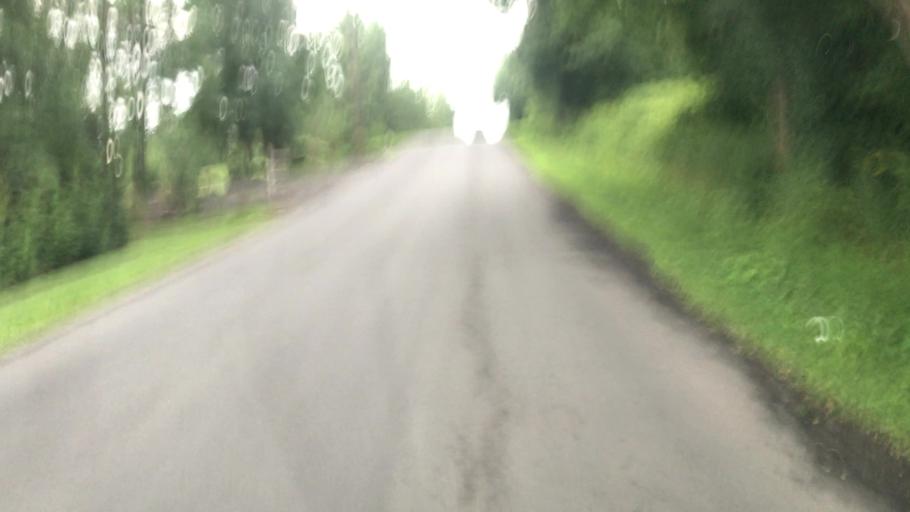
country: US
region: New York
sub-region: Cayuga County
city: Melrose Park
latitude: 42.9379
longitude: -76.5091
